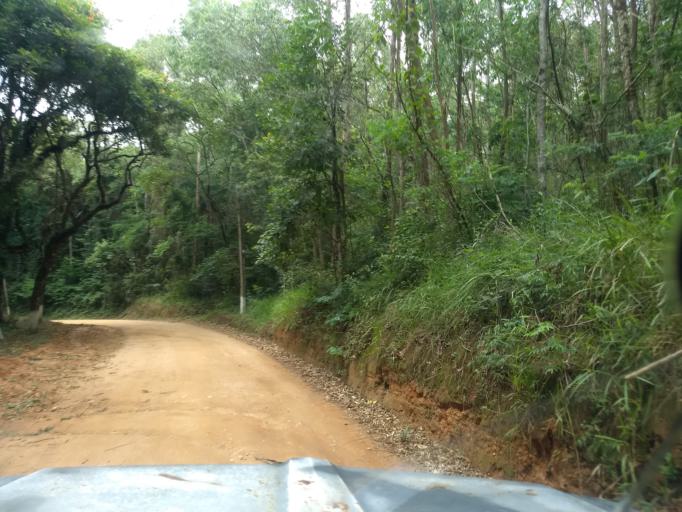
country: BR
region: Sao Paulo
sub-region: Cabreuva
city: Cabreuva
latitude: -23.3841
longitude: -47.1750
